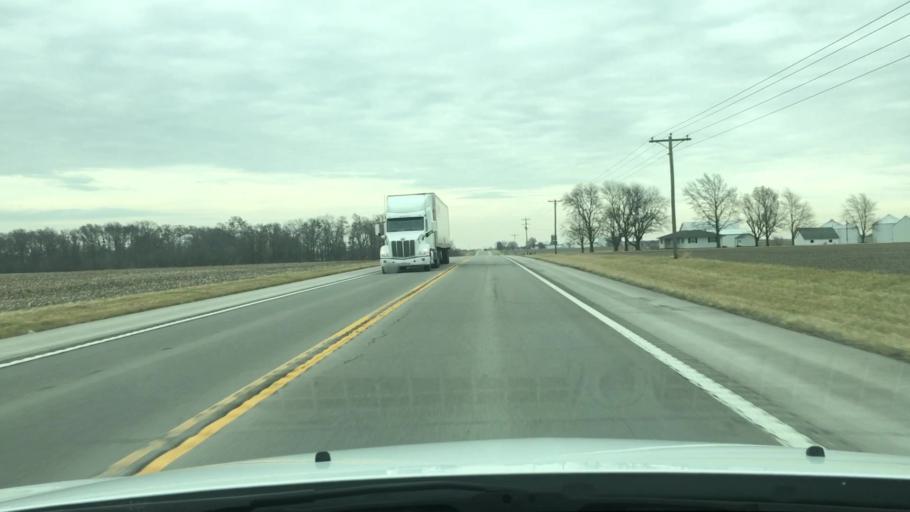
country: US
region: Missouri
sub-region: Audrain County
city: Mexico
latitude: 39.1638
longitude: -91.7546
